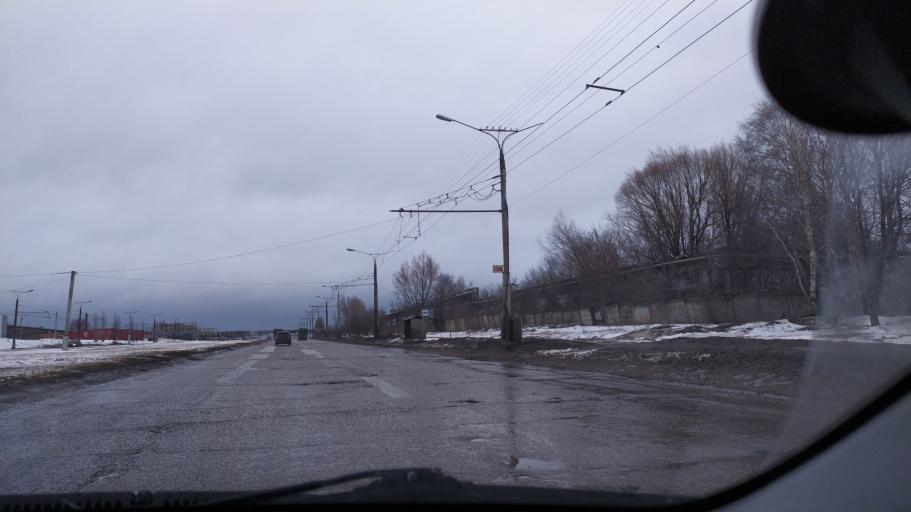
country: RU
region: Chuvashia
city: Kugesi
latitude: 56.1141
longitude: 47.3598
